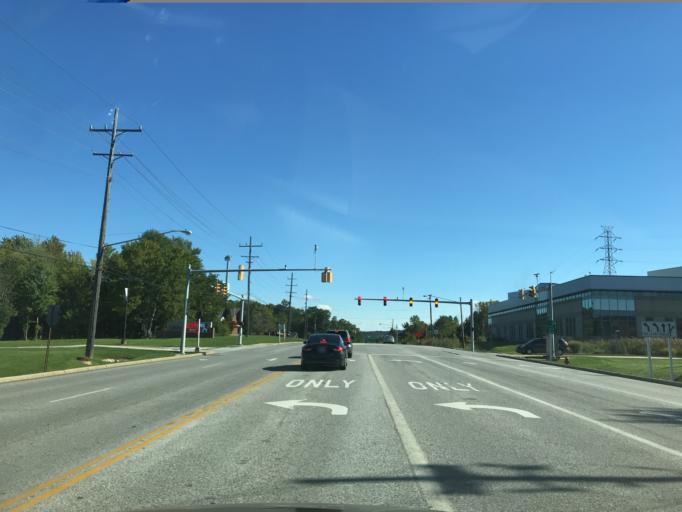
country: US
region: Ohio
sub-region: Lake County
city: Kirtland
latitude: 41.6372
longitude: -81.3709
